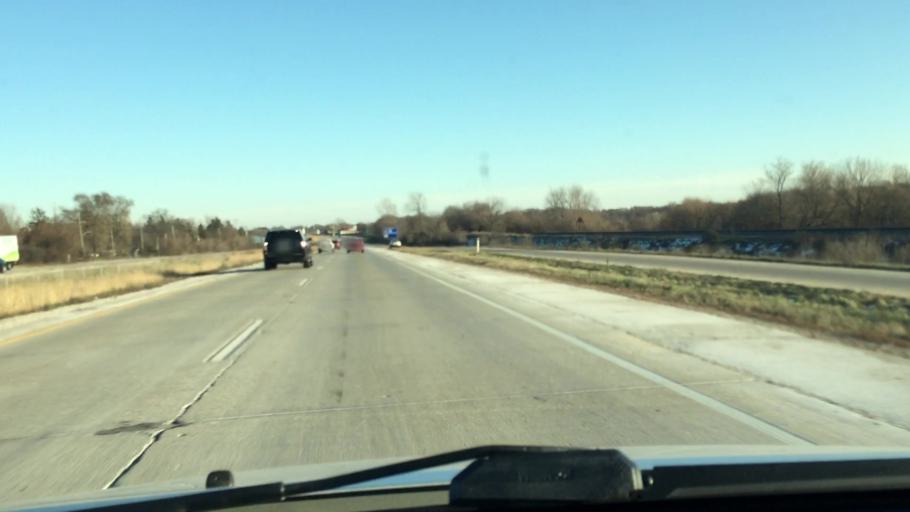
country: US
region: Wisconsin
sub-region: Waukesha County
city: Okauchee Lake
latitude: 43.1065
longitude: -88.4292
